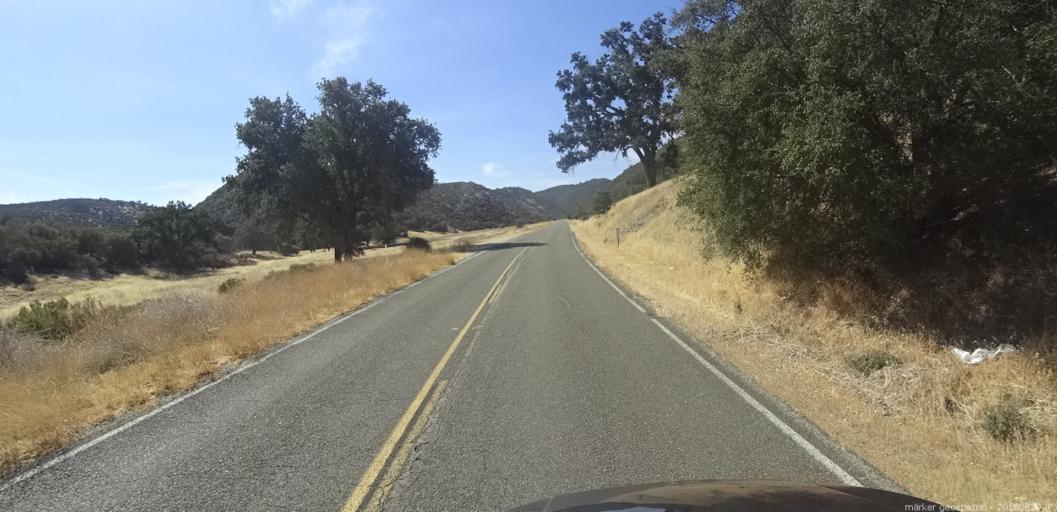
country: US
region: California
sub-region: San Luis Obispo County
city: Lake Nacimiento
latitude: 35.8714
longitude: -121.0631
